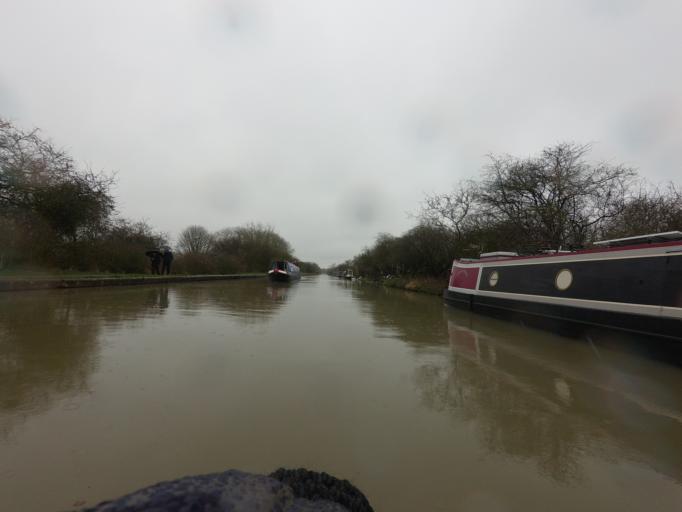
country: GB
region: England
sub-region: Milton Keynes
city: Stony Stratford
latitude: 52.0700
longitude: -0.8359
